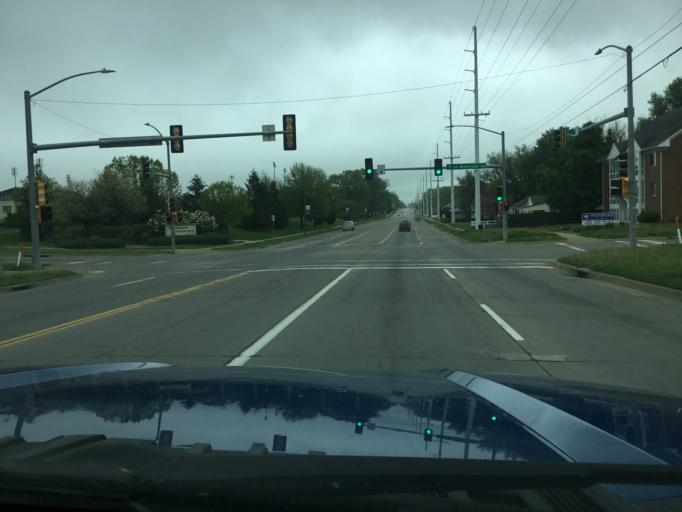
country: US
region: Kansas
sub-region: Shawnee County
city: Topeka
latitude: 39.0297
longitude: -95.7067
